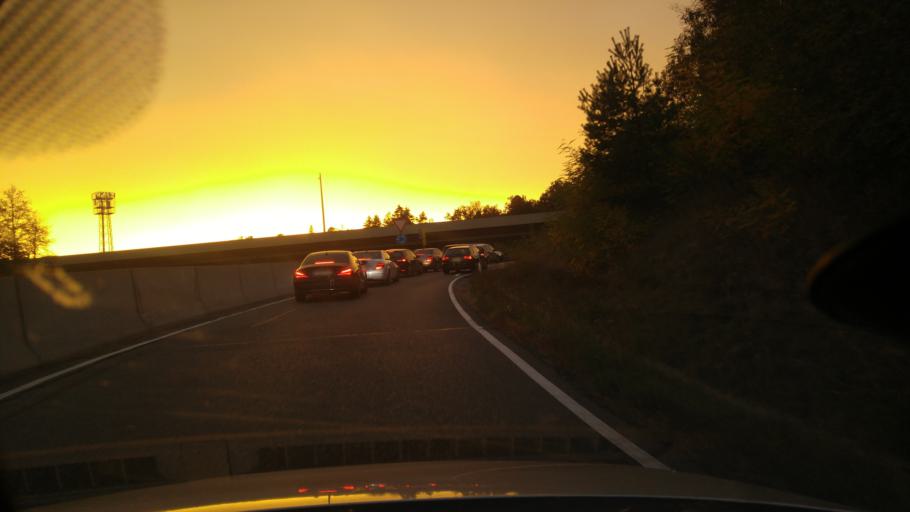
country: DE
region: Baden-Wuerttemberg
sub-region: Regierungsbezirk Stuttgart
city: Stuttgart Feuerbach
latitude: 48.7587
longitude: 9.1182
